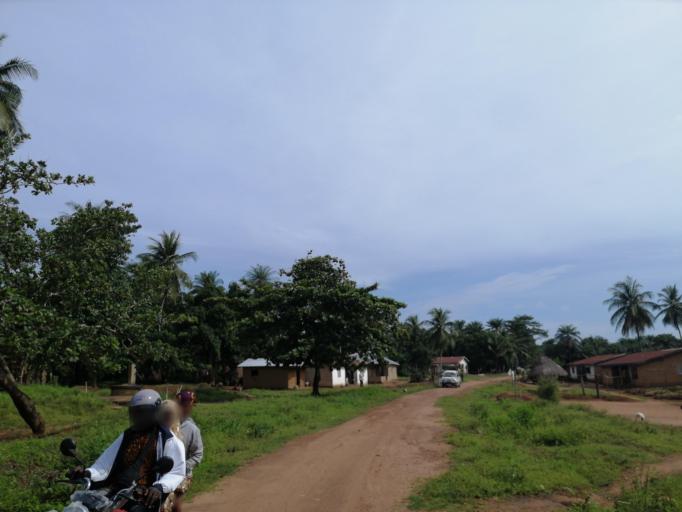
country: SL
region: Northern Province
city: Port Loko
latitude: 8.7869
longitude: -12.9249
